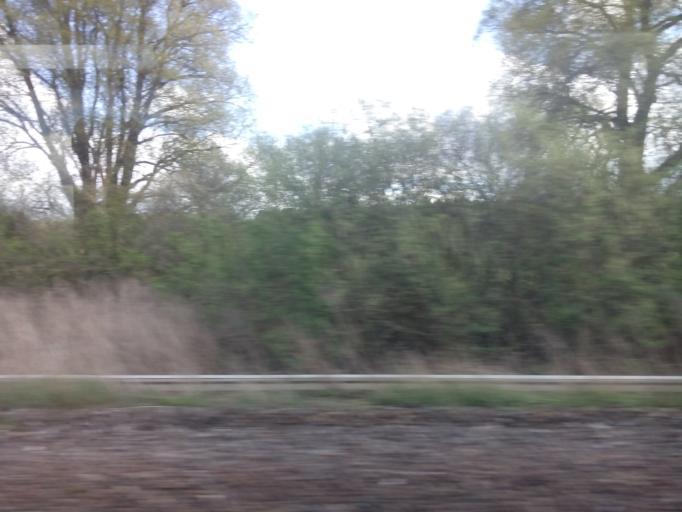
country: DE
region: Brandenburg
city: Velten
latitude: 52.6331
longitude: 13.1303
